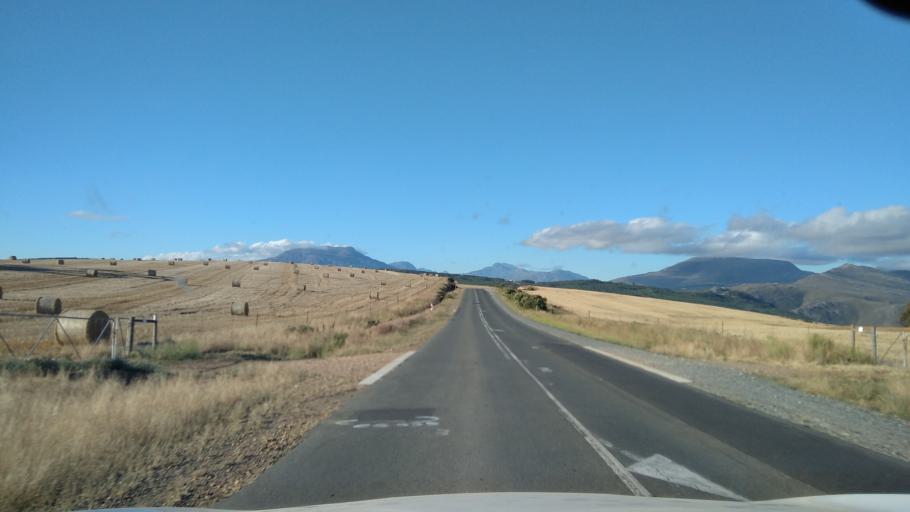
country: ZA
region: Western Cape
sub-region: Overberg District Municipality
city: Caledon
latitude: -34.1327
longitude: 19.2959
